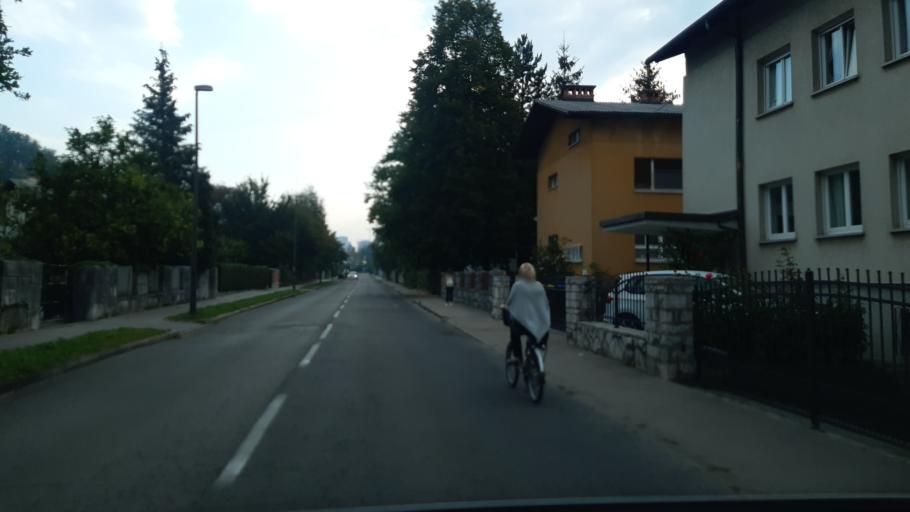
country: SI
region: Ljubljana
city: Ljubljana
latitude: 46.0500
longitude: 14.4894
